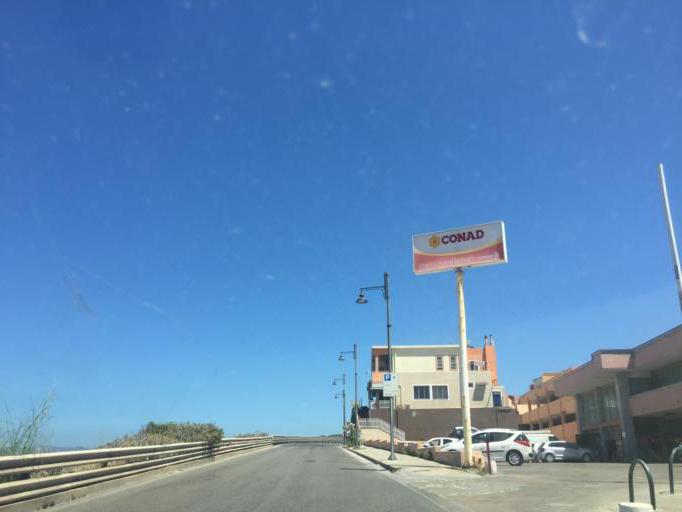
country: IT
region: Sardinia
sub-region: Provincia di Sassari
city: Castelsardo
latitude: 40.9126
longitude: 8.7147
